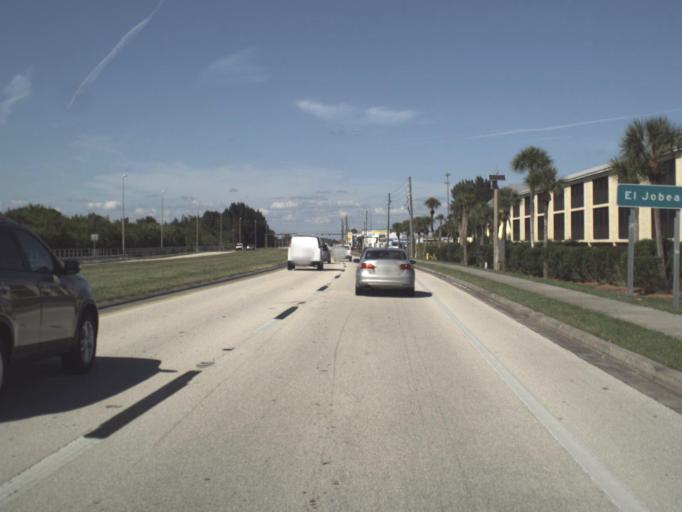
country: US
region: Florida
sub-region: Sarasota County
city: North Port
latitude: 26.9618
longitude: -82.2116
